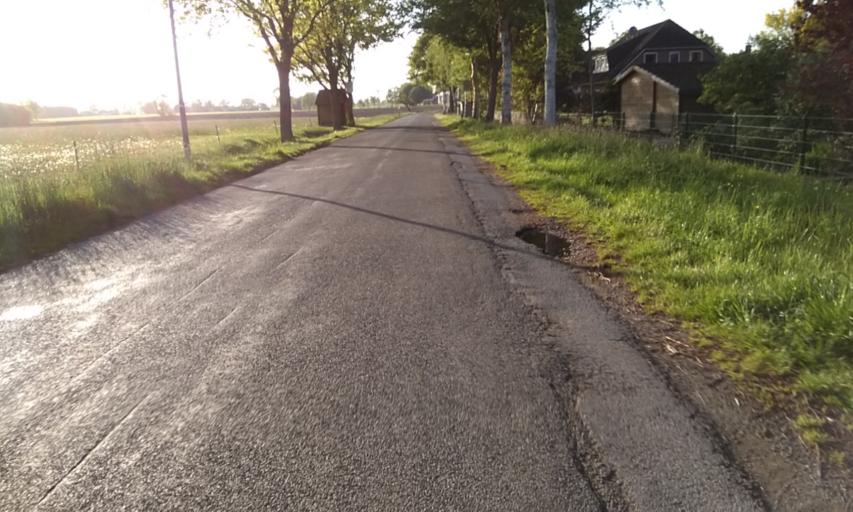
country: DE
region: Lower Saxony
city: Wohnste
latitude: 53.3950
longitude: 9.5051
